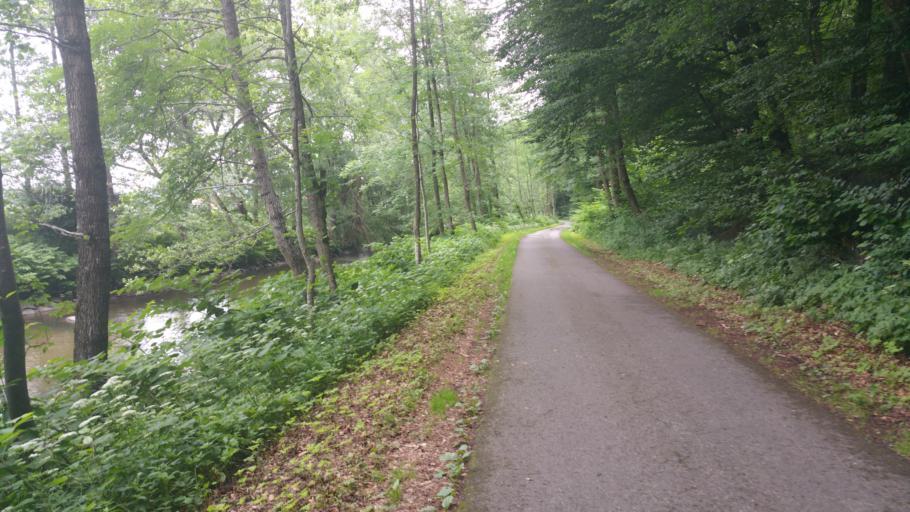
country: AT
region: Styria
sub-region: Politischer Bezirk Leibnitz
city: Gleinstatten
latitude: 46.7347
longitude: 15.3404
